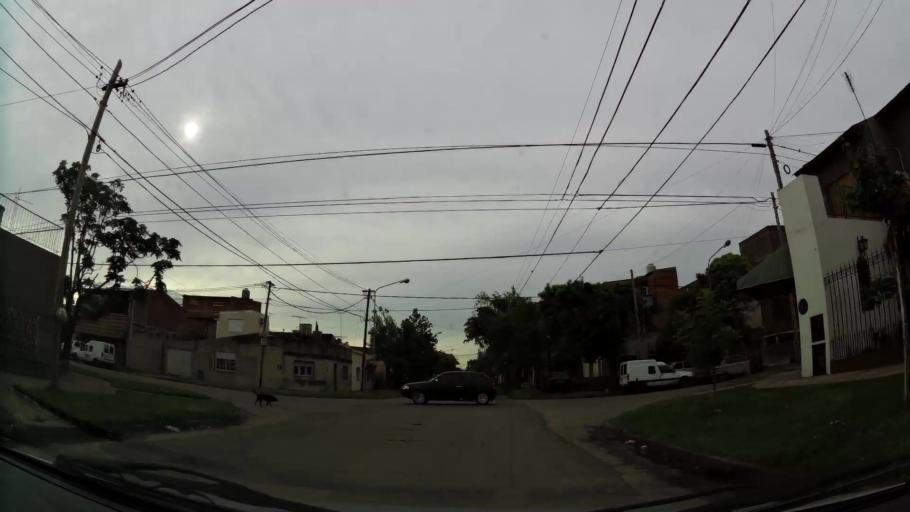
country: AR
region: Buenos Aires
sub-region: Partido de Lanus
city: Lanus
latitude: -34.7144
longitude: -58.3628
